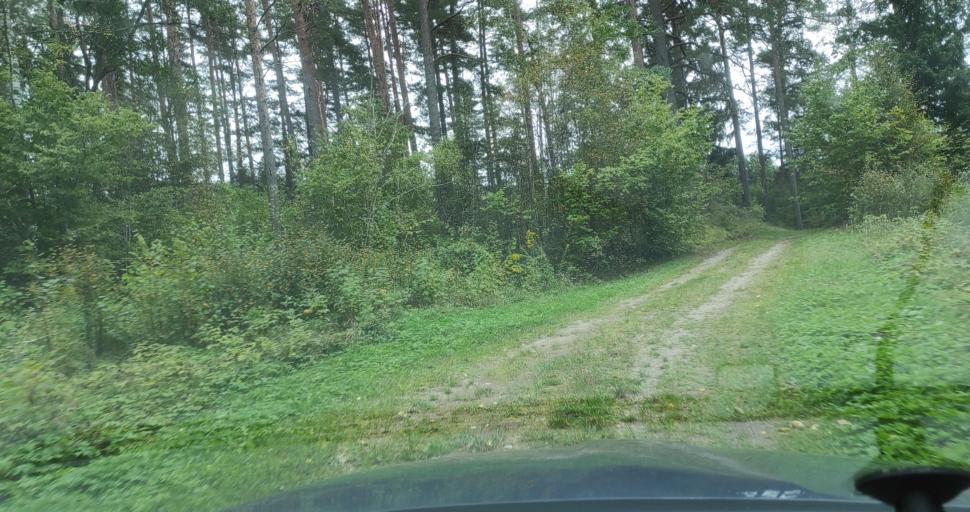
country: LV
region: Talsu Rajons
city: Stende
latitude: 57.0741
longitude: 22.3009
